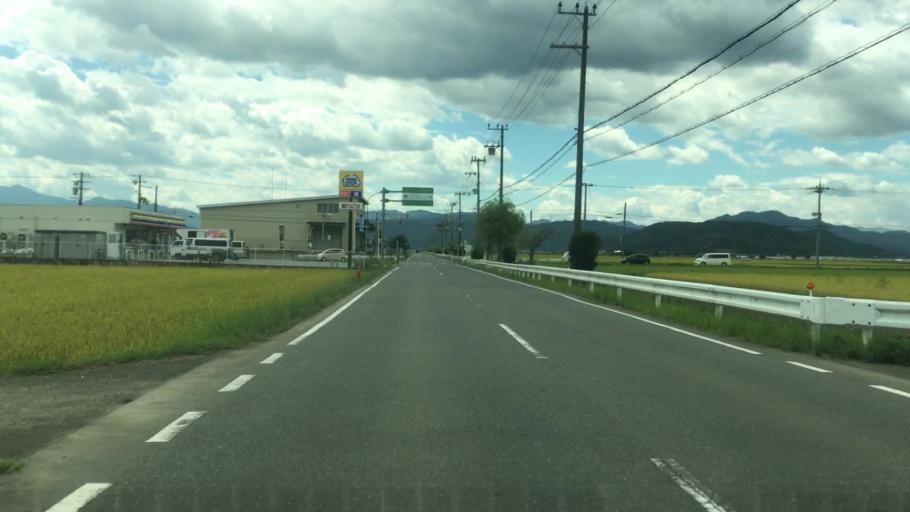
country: JP
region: Hyogo
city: Toyooka
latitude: 35.5257
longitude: 134.8398
